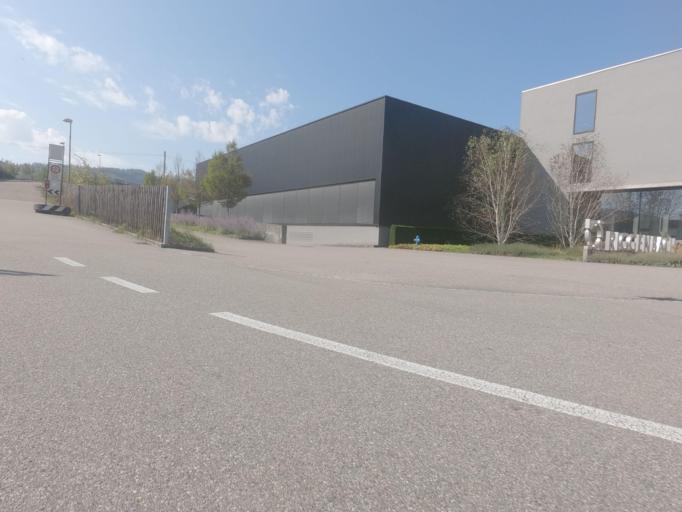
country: CH
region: Solothurn
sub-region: Bezirk Olten
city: Olten
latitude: 47.3500
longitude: 7.8951
